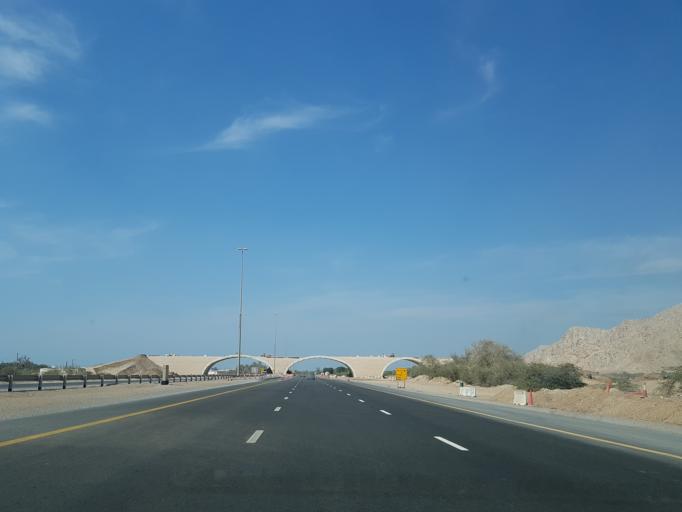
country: AE
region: Ra's al Khaymah
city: Ras al-Khaimah
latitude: 25.8184
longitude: 56.0256
